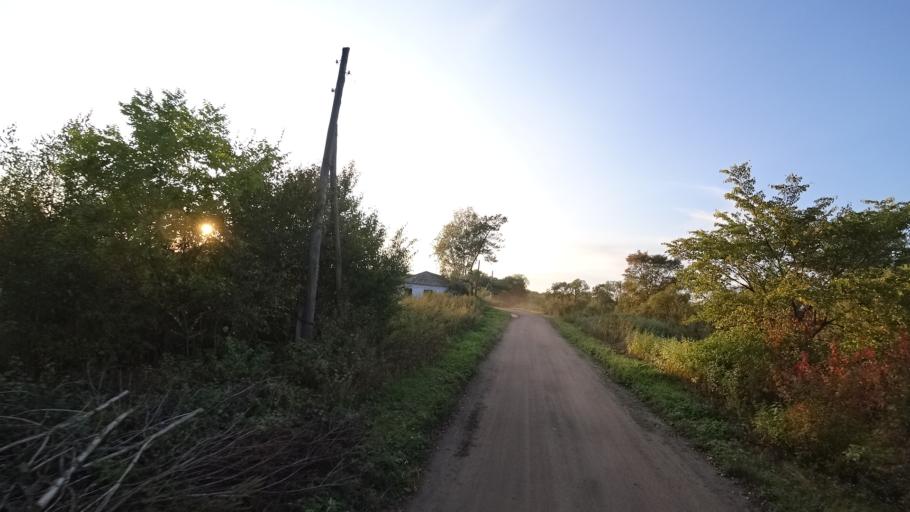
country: RU
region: Amur
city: Arkhara
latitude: 49.3651
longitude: 130.1161
